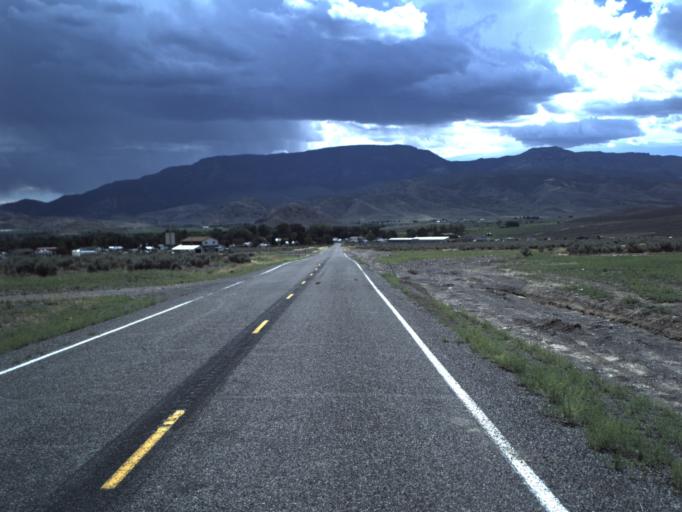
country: US
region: Utah
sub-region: Piute County
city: Junction
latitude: 38.2456
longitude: -112.2343
